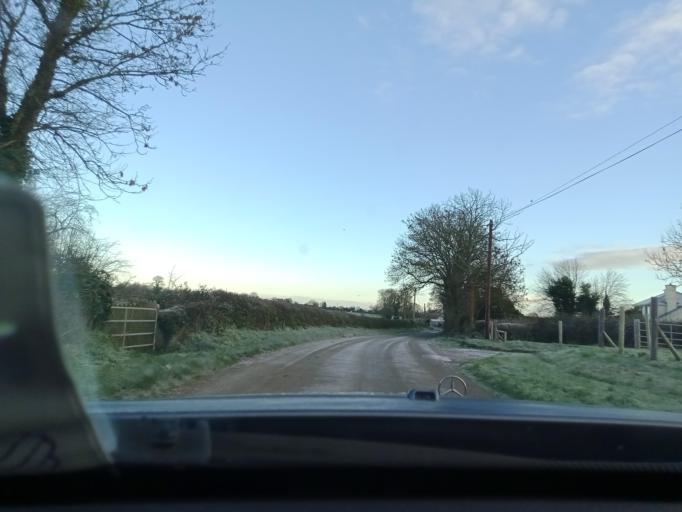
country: IE
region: Leinster
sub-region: County Carlow
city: Bagenalstown
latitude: 52.6394
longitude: -7.0245
